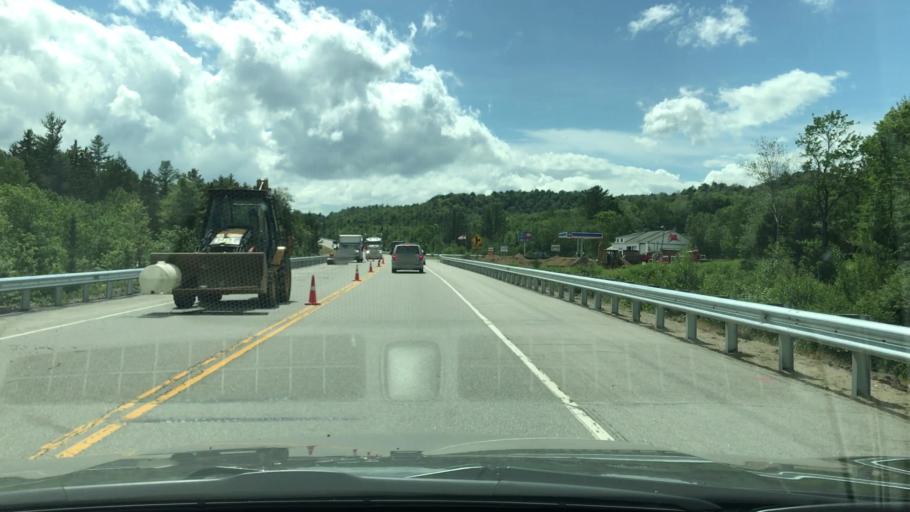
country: US
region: New Hampshire
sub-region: Coos County
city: Gorham
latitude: 44.3650
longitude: -71.3270
